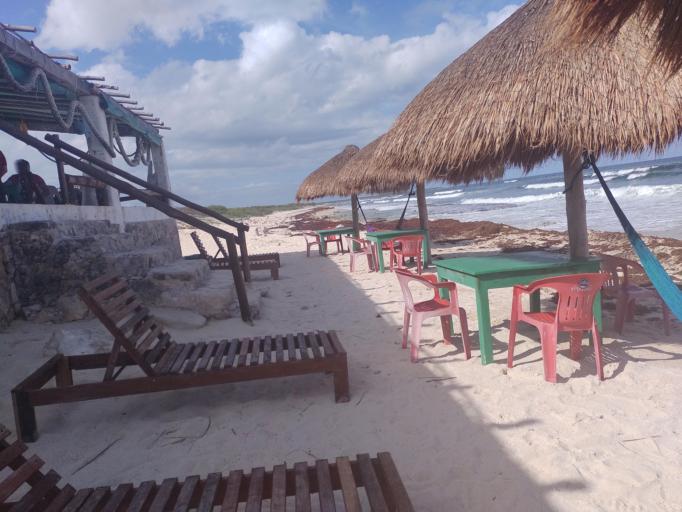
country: MX
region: Quintana Roo
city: San Miguel de Cozumel
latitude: 20.4237
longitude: -86.8428
